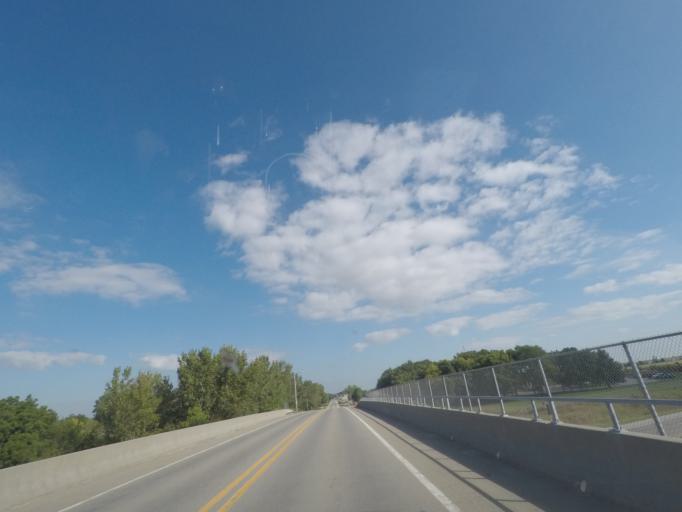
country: US
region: Iowa
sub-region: Story County
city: Nevada
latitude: 42.0056
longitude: -93.4445
